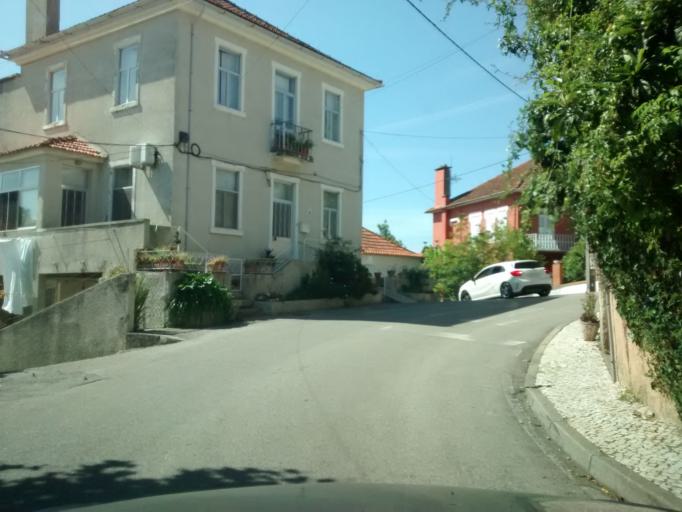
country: PT
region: Aveiro
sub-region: Mealhada
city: Pampilhosa do Botao
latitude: 40.3829
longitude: -8.3795
